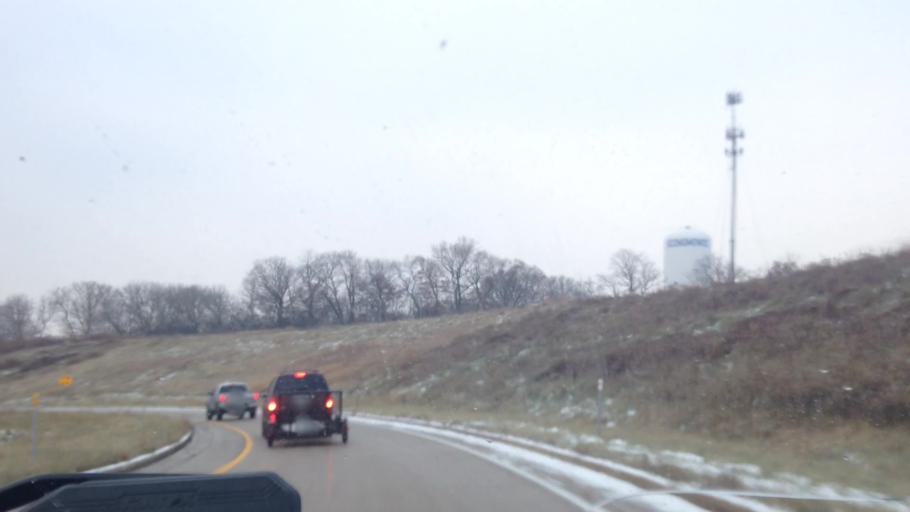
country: US
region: Wisconsin
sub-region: Waukesha County
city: Oconomowoc
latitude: 43.1101
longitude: -88.4809
